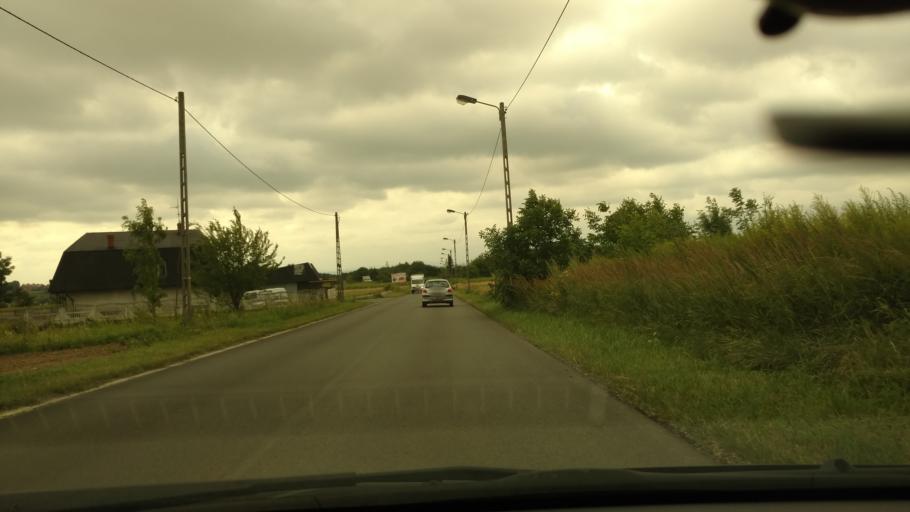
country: PL
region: Lesser Poland Voivodeship
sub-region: Powiat krakowski
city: Zielonki
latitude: 50.1157
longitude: 19.9423
